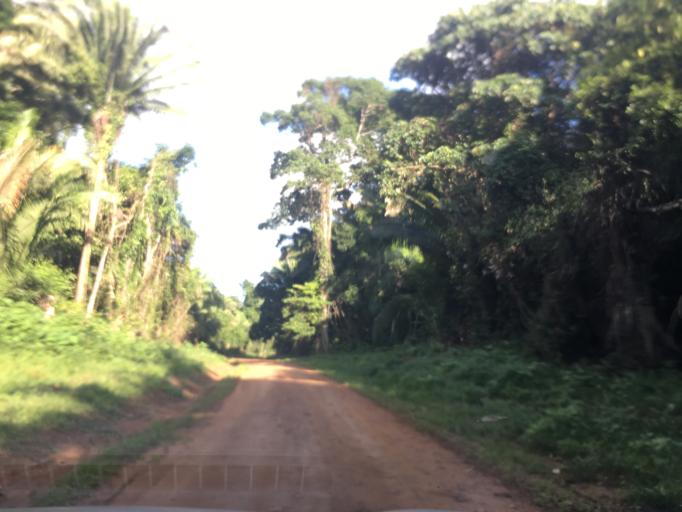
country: BZ
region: Stann Creek
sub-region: Dangriga
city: Dangriga
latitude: 16.7931
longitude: -88.4317
